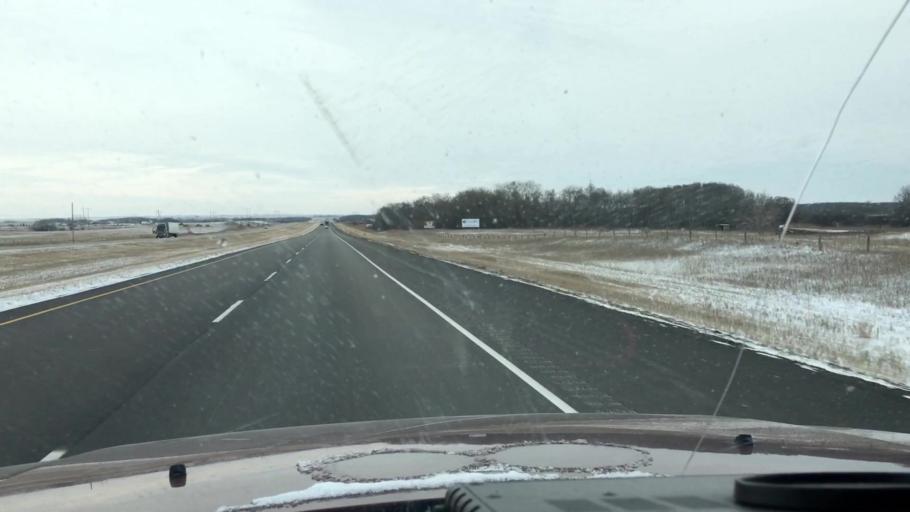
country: CA
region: Saskatchewan
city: Saskatoon
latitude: 51.9030
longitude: -106.5228
